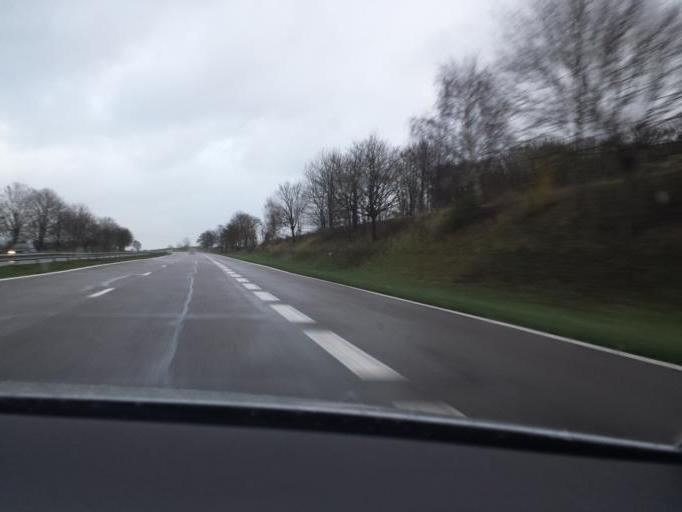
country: FR
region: Haute-Normandie
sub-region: Departement de l'Eure
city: Pacy-sur-Eure
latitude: 49.0080
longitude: 1.3979
